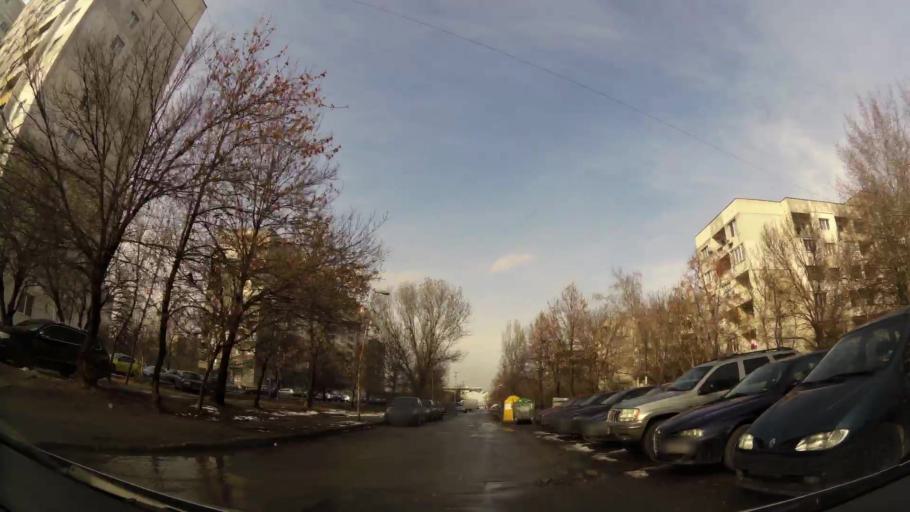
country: BG
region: Sofia-Capital
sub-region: Stolichna Obshtina
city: Sofia
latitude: 42.7155
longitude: 23.2654
